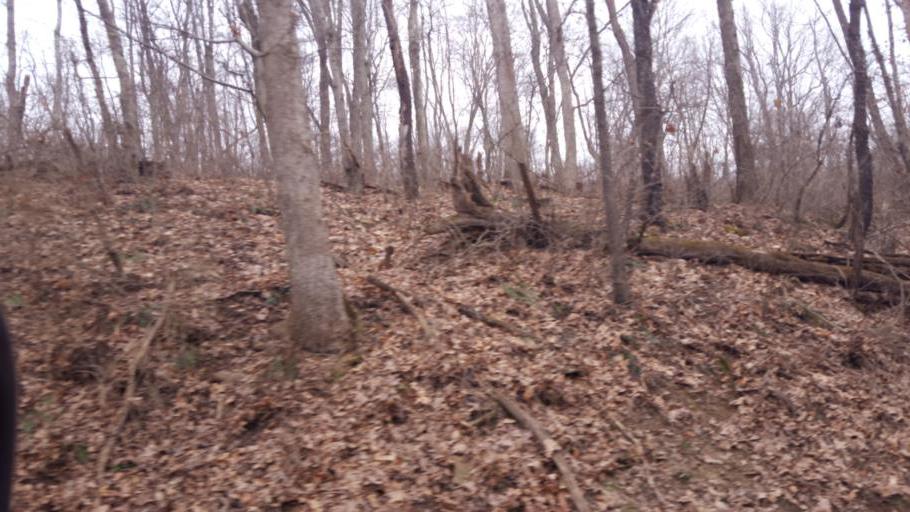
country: US
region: Ohio
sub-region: Ashland County
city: Loudonville
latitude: 40.5724
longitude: -82.2268
